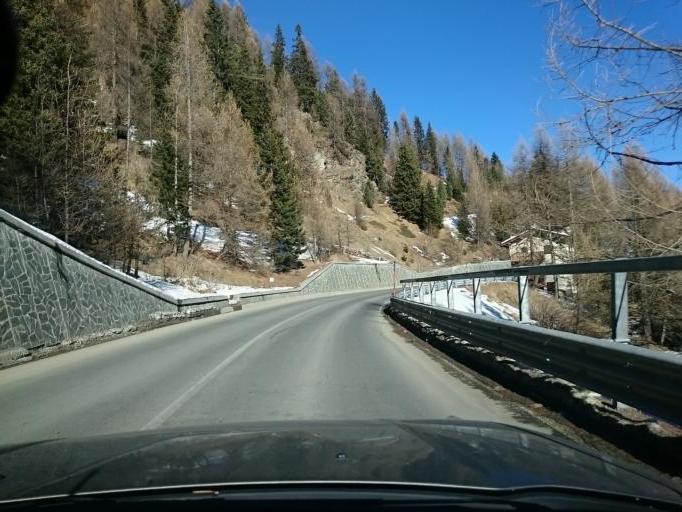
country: IT
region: Lombardy
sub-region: Provincia di Sondrio
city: Isolaccia
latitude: 46.4672
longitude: 10.2467
